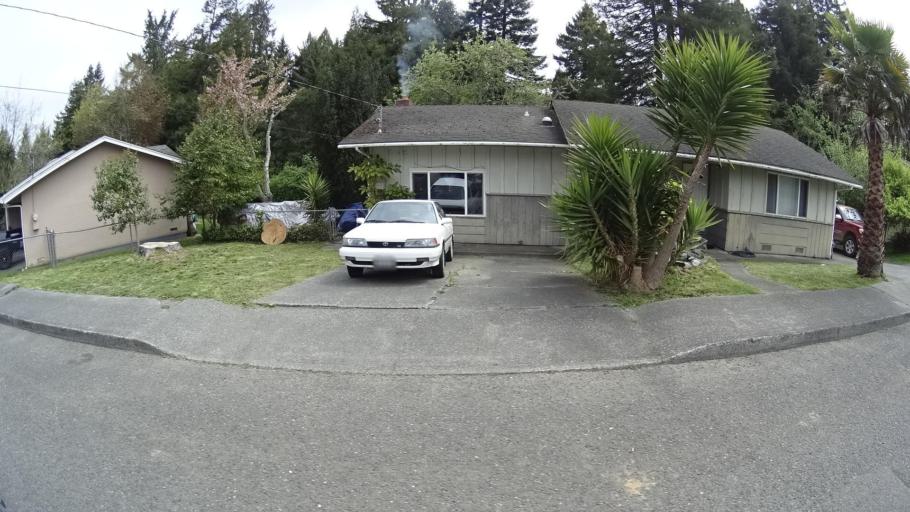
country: US
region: California
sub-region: Humboldt County
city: Cutten
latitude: 40.7657
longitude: -124.1498
